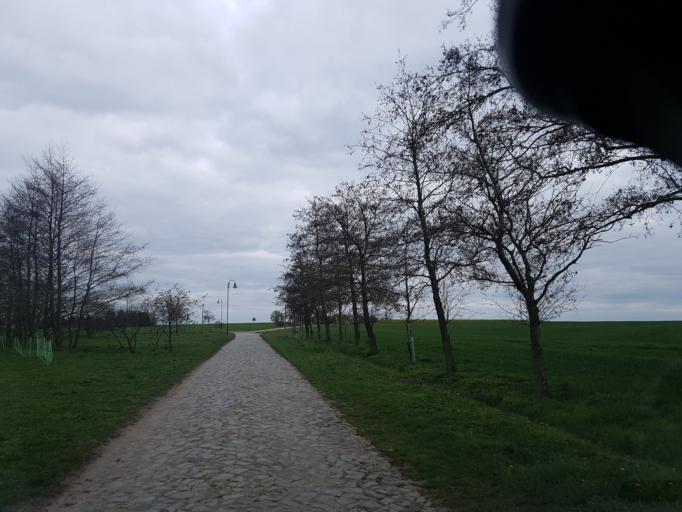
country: DE
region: Brandenburg
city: Juterbog
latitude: 51.9143
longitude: 13.0967
